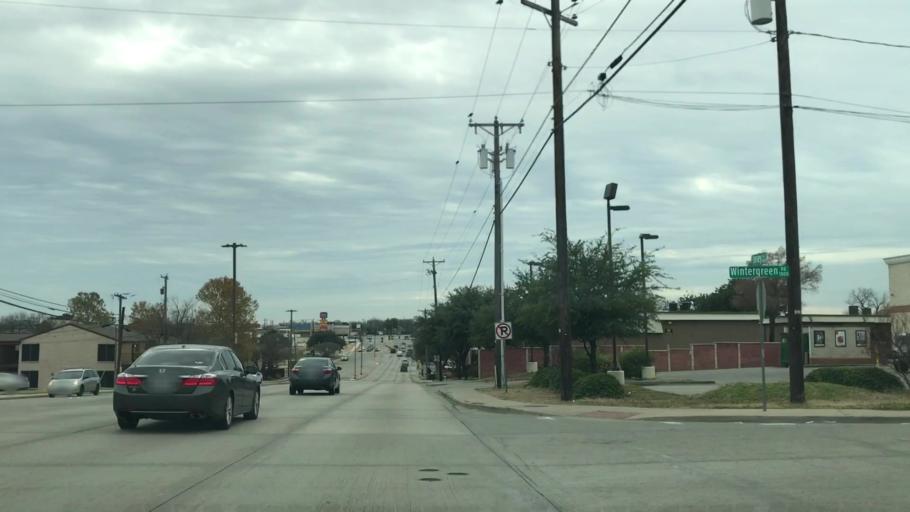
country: US
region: Texas
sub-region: Dallas County
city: Carrollton
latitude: 32.9415
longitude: -96.8906
